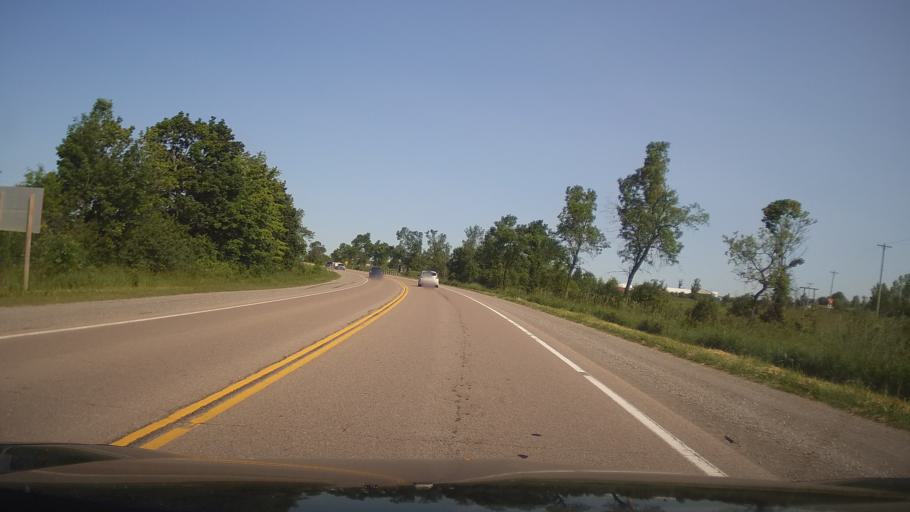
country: CA
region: Ontario
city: Omemee
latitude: 44.3424
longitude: -78.7656
